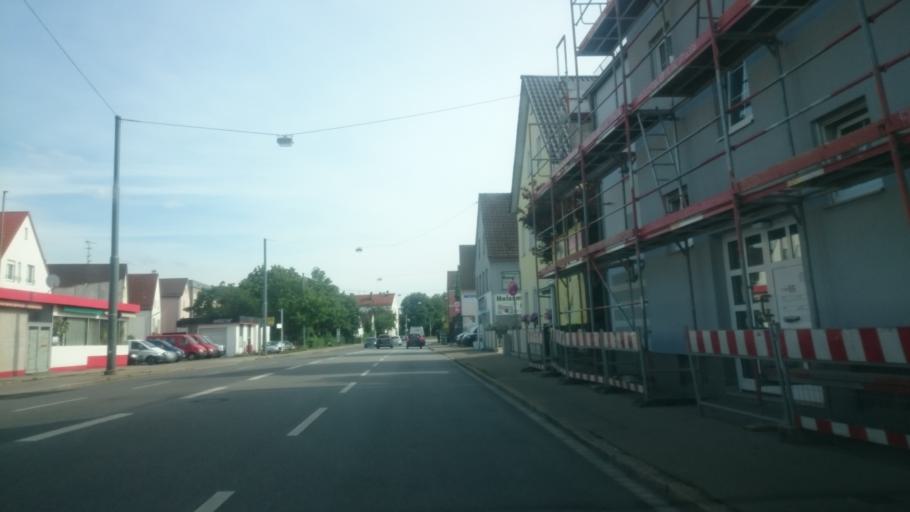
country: DE
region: Bavaria
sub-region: Swabia
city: Augsburg
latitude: 48.3855
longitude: 10.9172
